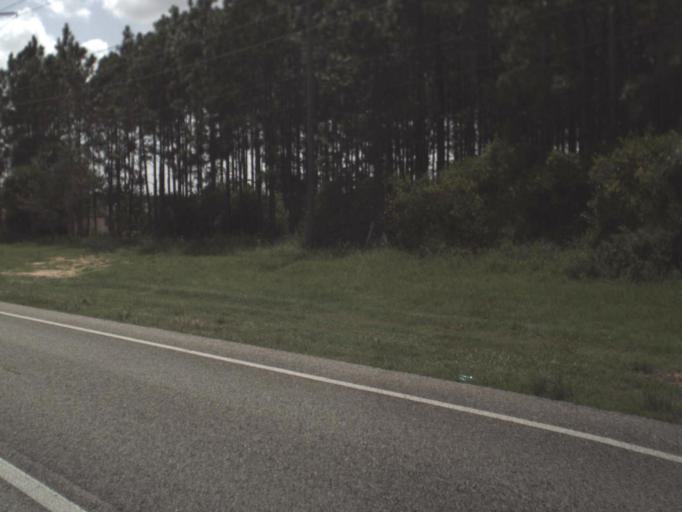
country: US
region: Florida
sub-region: Lake County
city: Four Corners
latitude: 28.3149
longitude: -81.6684
